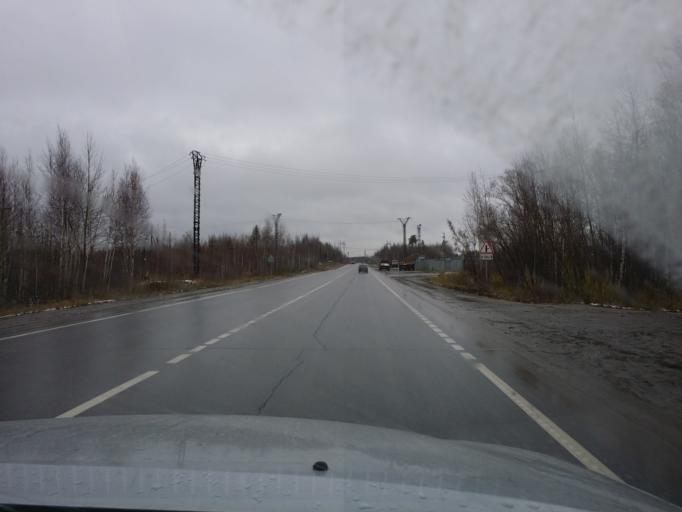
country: RU
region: Khanty-Mansiyskiy Avtonomnyy Okrug
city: Megion
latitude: 61.0739
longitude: 76.1166
